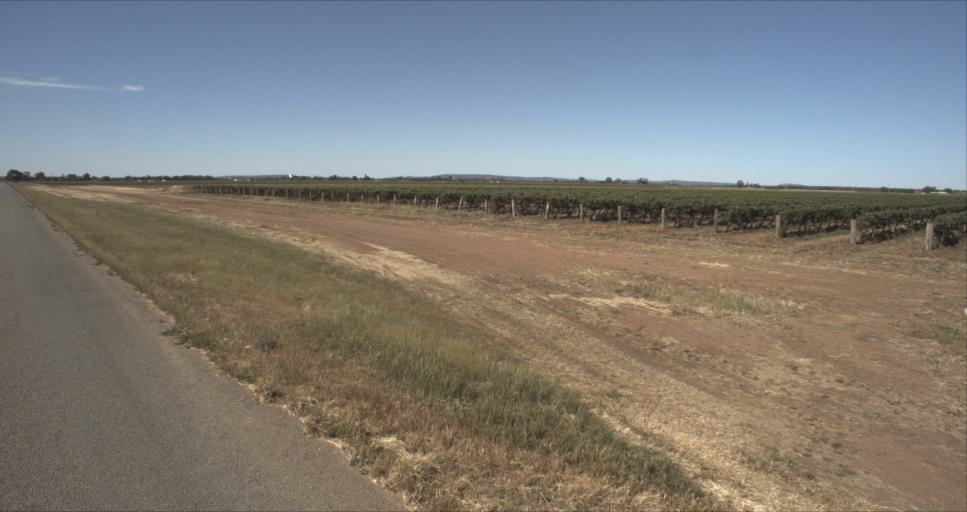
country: AU
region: New South Wales
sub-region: Leeton
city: Leeton
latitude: -34.5844
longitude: 146.3792
